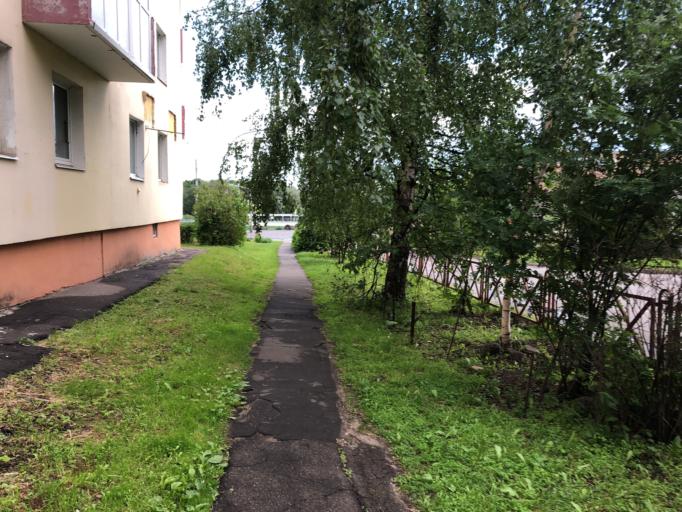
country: RU
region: Jaroslavl
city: Yaroslavl
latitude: 57.6206
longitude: 39.8799
